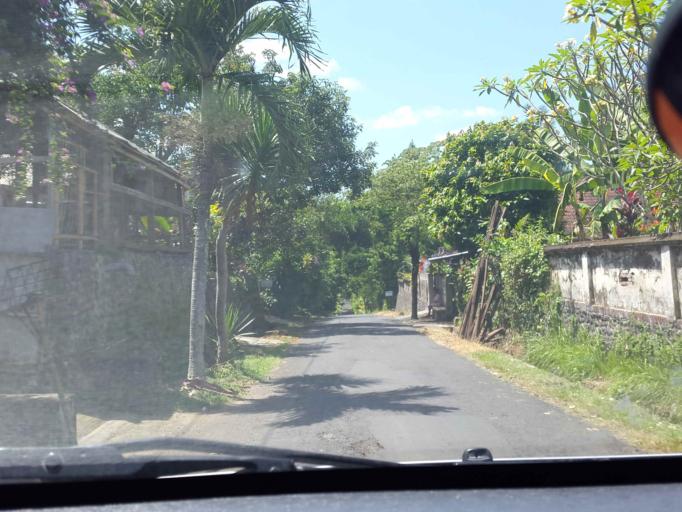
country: ID
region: Bali
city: Banjar Wangsian
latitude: -8.4980
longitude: 115.3993
